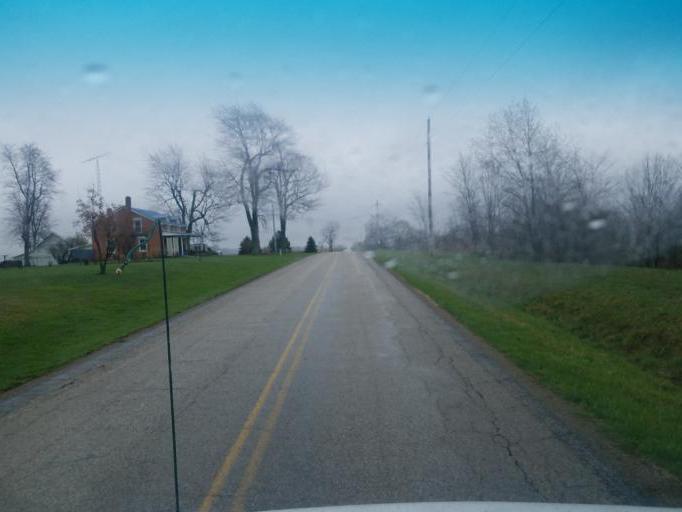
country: US
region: Ohio
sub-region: Crawford County
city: Bucyrus
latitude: 40.9651
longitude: -82.9959
